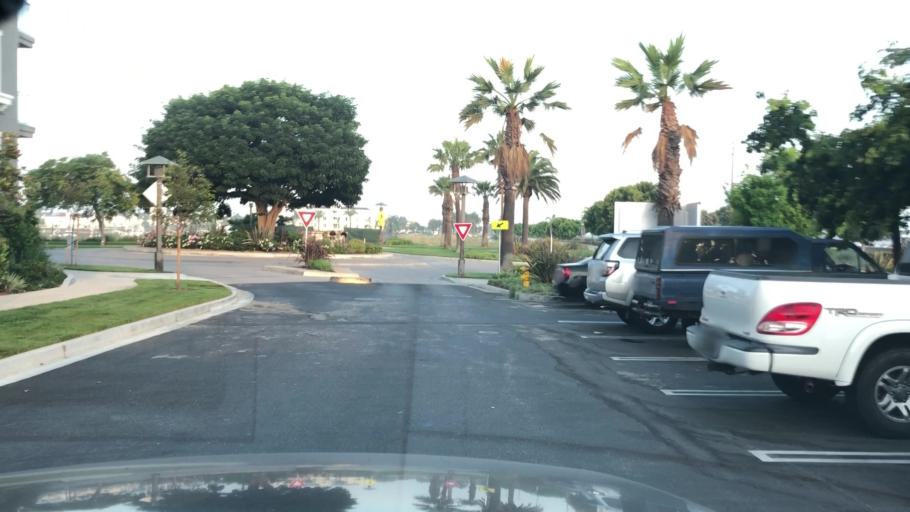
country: US
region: California
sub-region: Ventura County
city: Oxnard Shores
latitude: 34.1900
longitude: -119.2242
